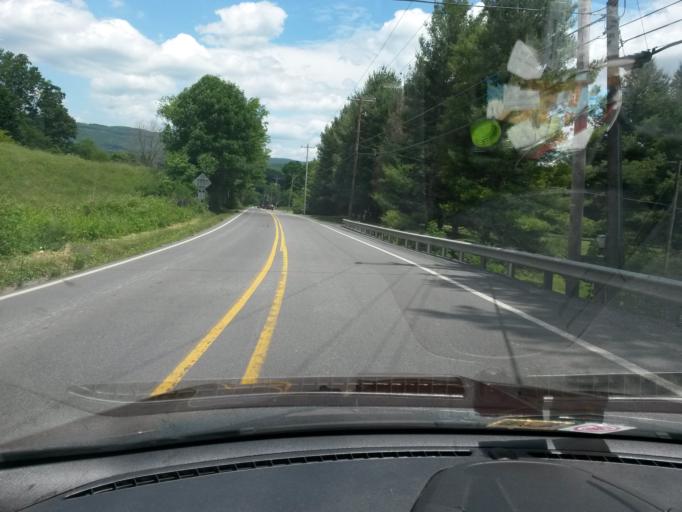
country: US
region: West Virginia
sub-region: Greenbrier County
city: Rainelle
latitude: 37.9529
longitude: -80.6680
